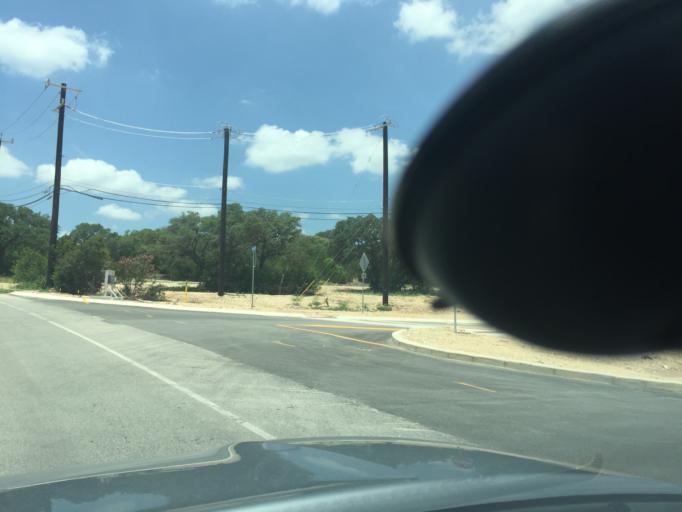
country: US
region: Texas
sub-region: Bexar County
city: Timberwood Park
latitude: 29.7154
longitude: -98.4724
